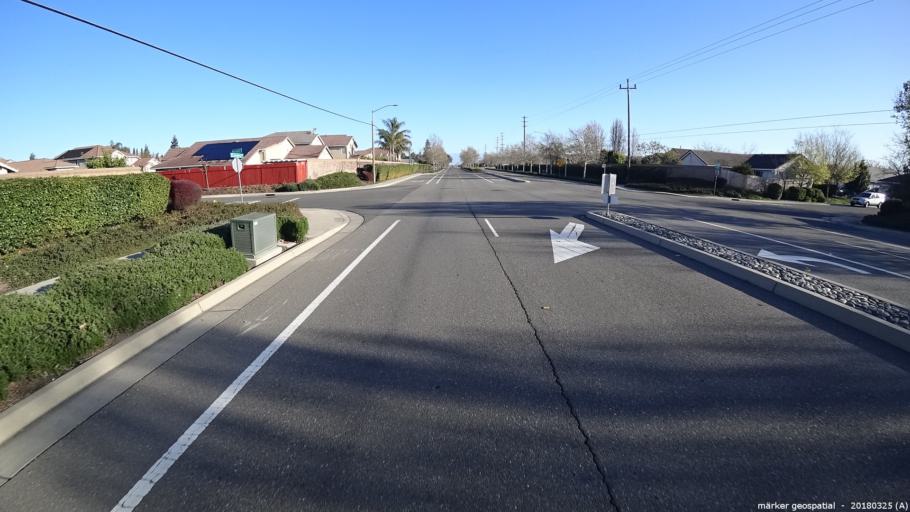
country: US
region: California
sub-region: Yolo County
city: West Sacramento
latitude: 38.6292
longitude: -121.5396
